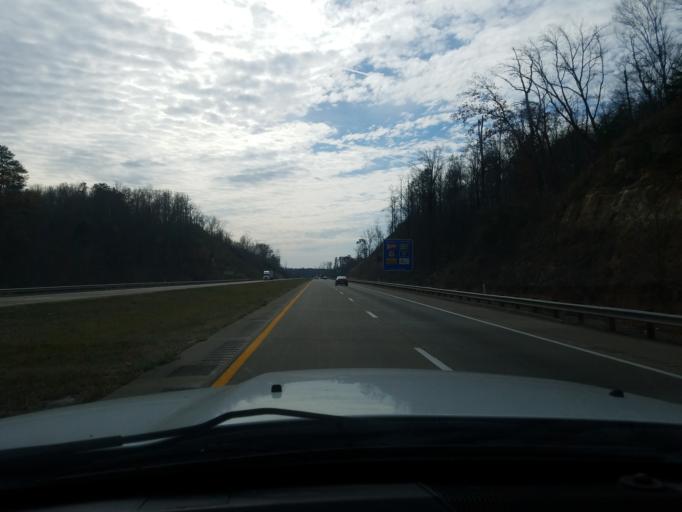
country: US
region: West Virginia
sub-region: Putnam County
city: Eleanor
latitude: 38.4967
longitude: -81.9322
